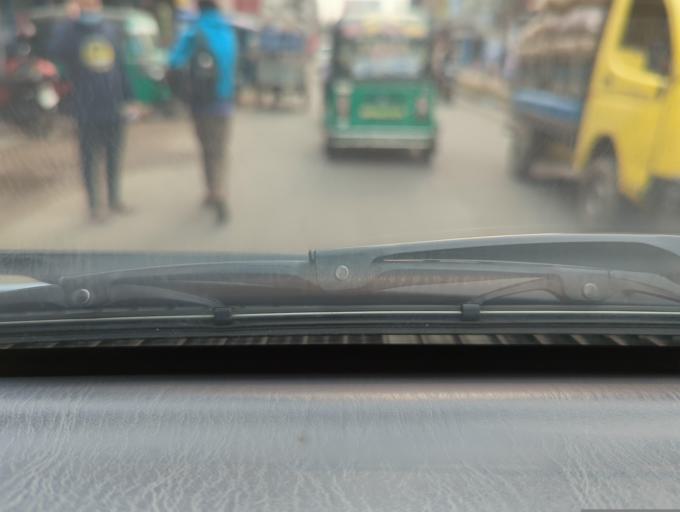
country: BD
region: Sylhet
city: Maulavi Bazar
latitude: 24.4849
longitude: 91.7656
